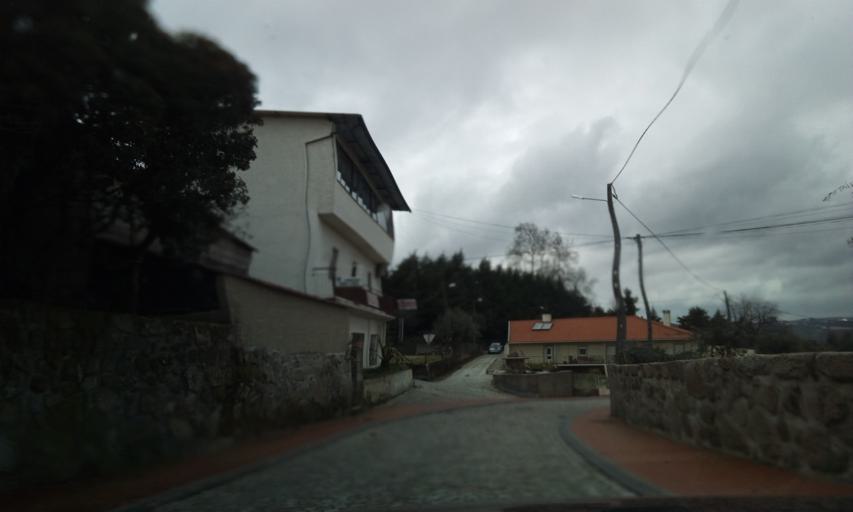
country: PT
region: Viseu
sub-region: Nelas
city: Nelas
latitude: 40.6008
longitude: -7.8450
